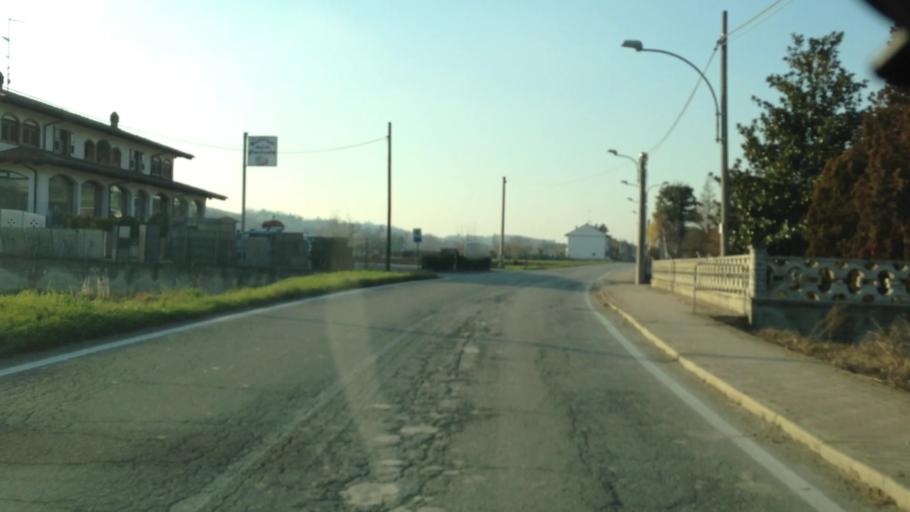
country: IT
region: Piedmont
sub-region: Provincia di Asti
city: Montegrosso
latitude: 44.8166
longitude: 8.2514
